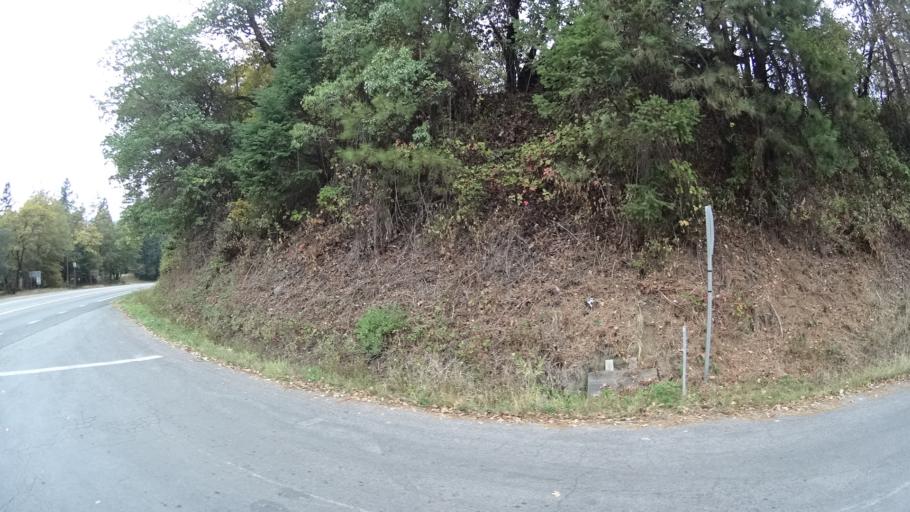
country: US
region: California
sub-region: Siskiyou County
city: Happy Camp
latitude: 41.7890
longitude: -123.3835
